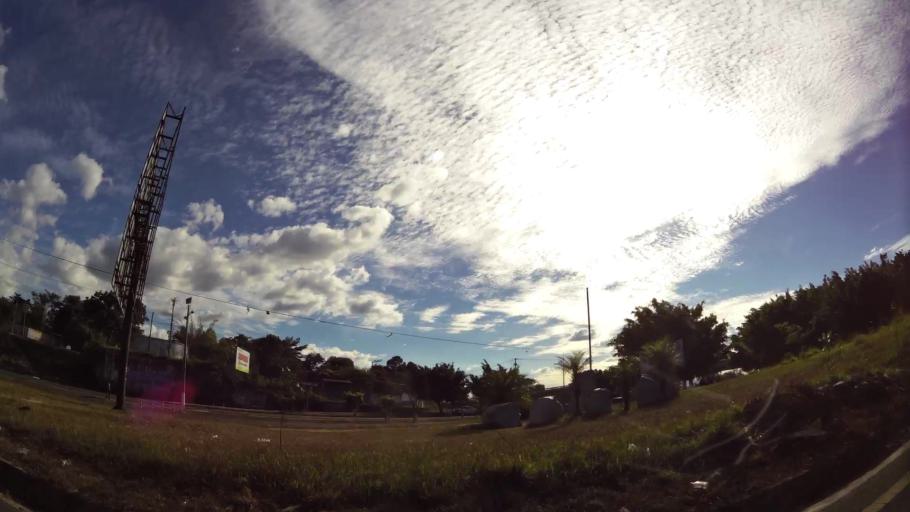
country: SV
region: San Salvador
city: Ilopango
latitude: 13.7340
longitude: -89.0648
